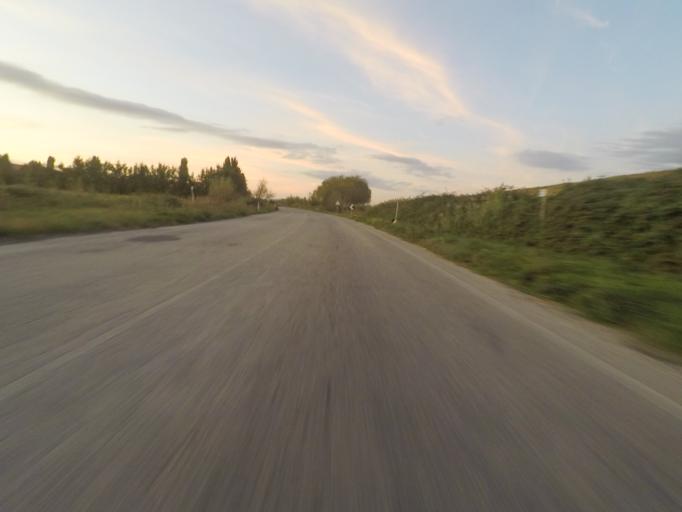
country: IT
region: Tuscany
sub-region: Provincia di Siena
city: Sinalunga
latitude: 43.2134
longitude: 11.7622
